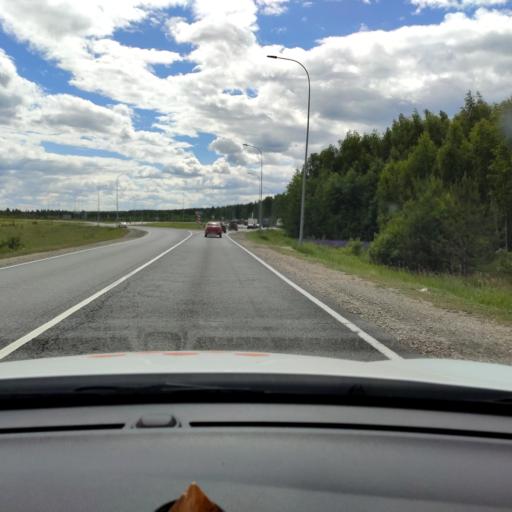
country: RU
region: Tatarstan
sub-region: Zelenodol'skiy Rayon
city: Zelenodolsk
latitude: 55.8928
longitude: 48.5431
